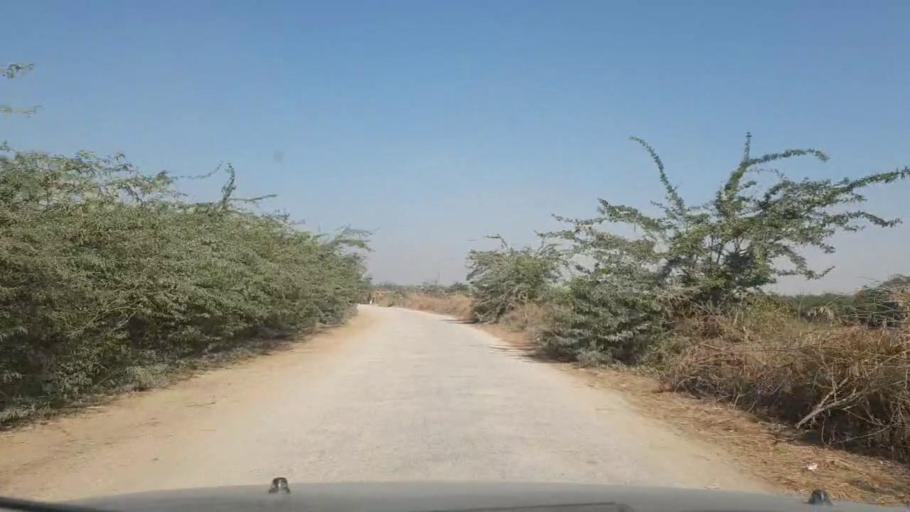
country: PK
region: Sindh
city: Thatta
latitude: 24.8013
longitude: 67.9021
